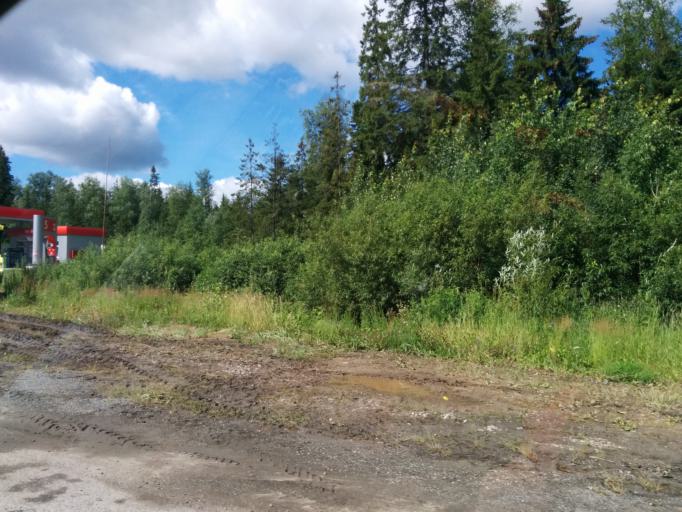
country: RU
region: Perm
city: Kondratovo
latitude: 58.0487
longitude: 56.0633
